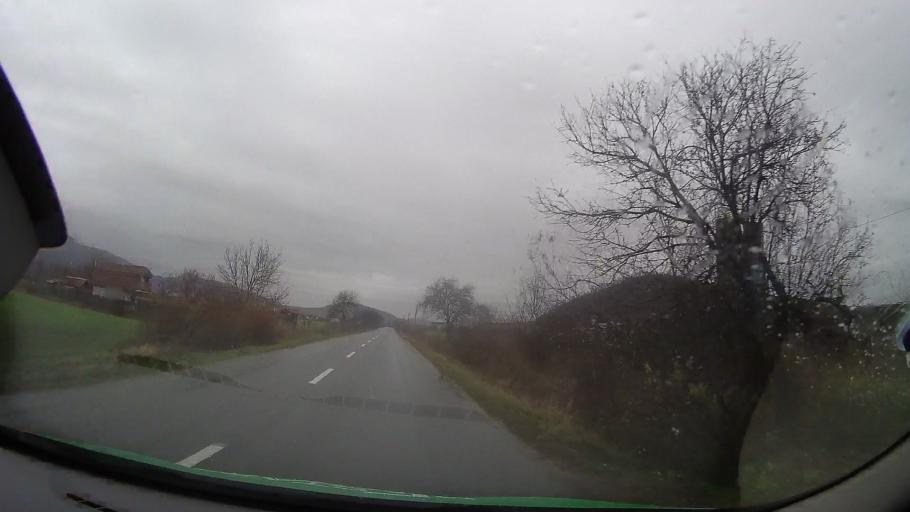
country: RO
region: Bistrita-Nasaud
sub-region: Municipiul Bistrita
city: Viisoara
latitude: 47.0626
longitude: 24.4366
